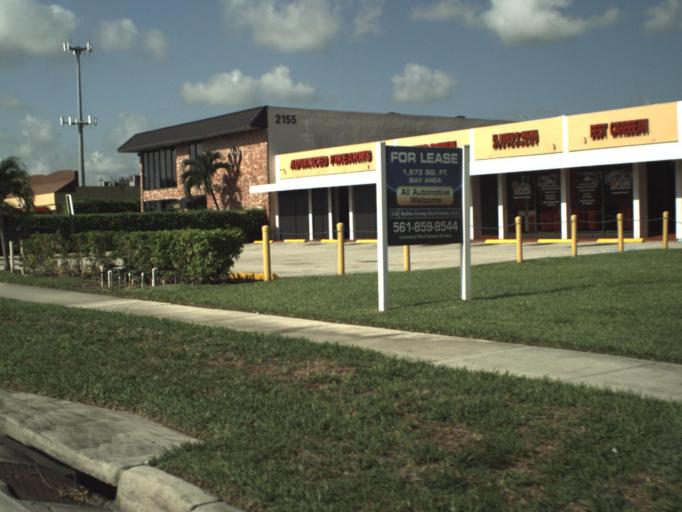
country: US
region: Florida
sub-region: Broward County
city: Margate
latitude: 26.2566
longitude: -80.2017
